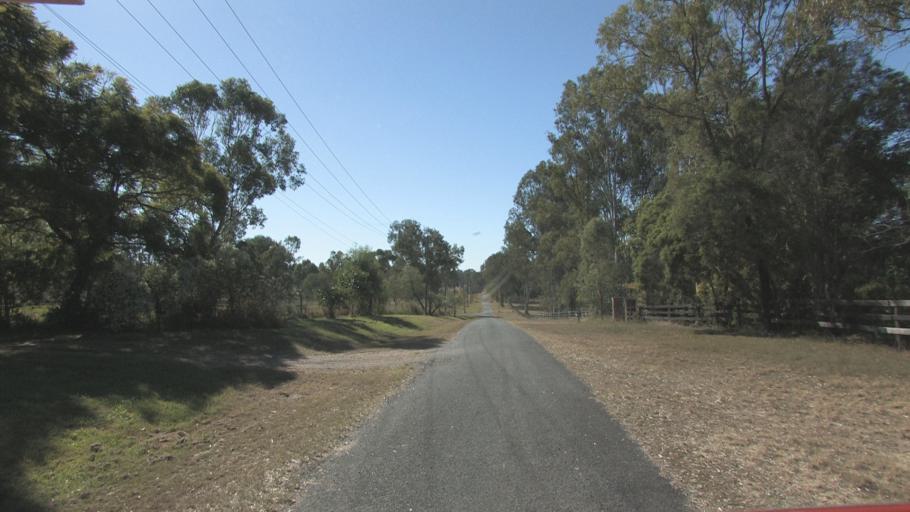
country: AU
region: Queensland
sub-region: Logan
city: North Maclean
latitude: -27.7785
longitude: 153.0245
